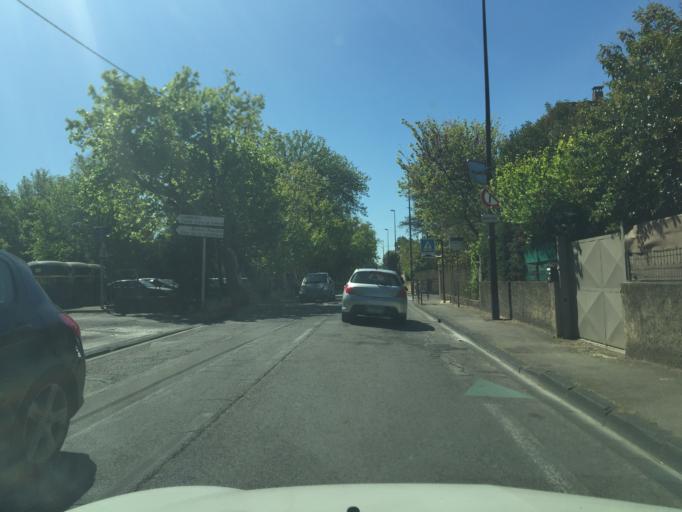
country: FR
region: Provence-Alpes-Cote d'Azur
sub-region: Departement du Vaucluse
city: Montfavet
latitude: 43.9378
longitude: 4.8709
